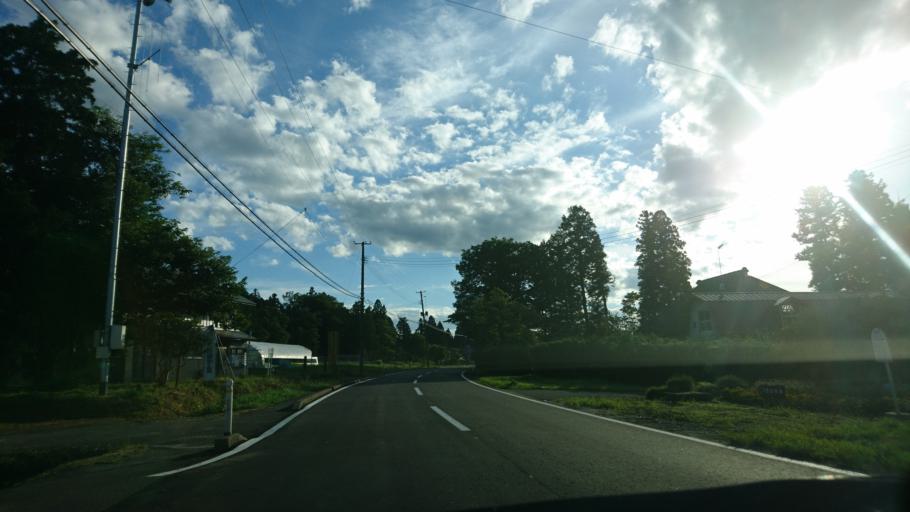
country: JP
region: Iwate
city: Ichinoseki
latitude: 38.8409
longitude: 141.1500
